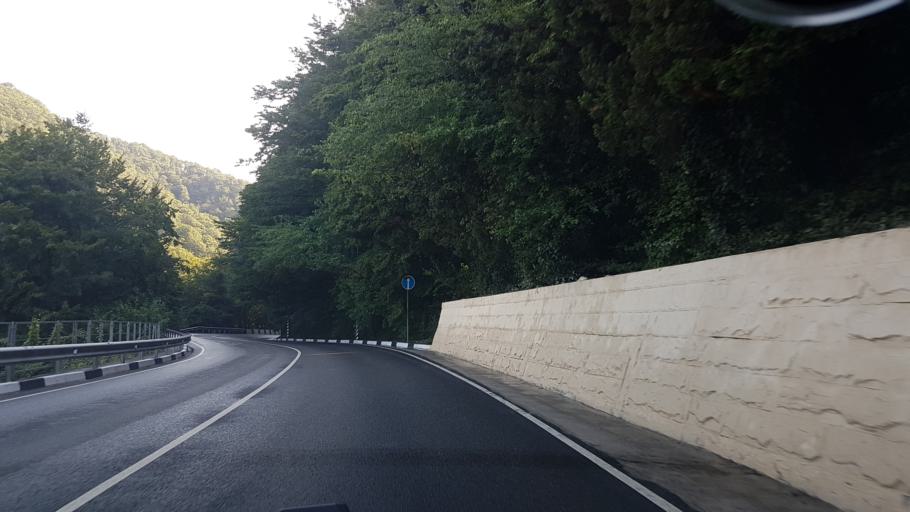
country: RU
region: Krasnodarskiy
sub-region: Sochi City
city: Lazarevskoye
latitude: 43.8366
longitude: 39.4194
